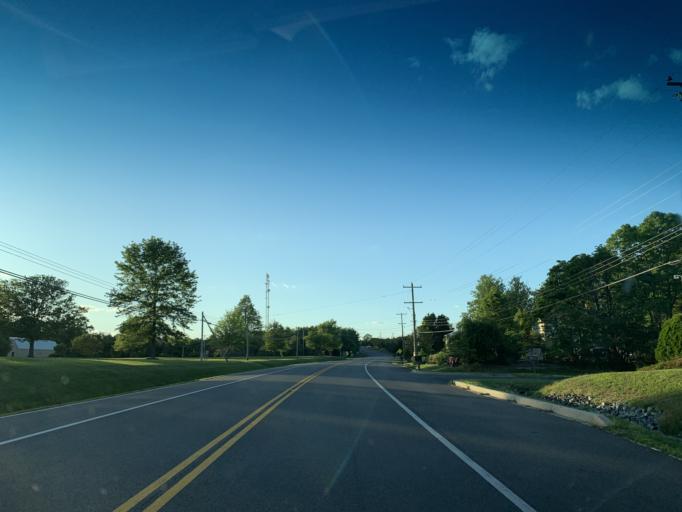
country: US
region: Maryland
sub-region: Cecil County
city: Elkton
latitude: 39.6742
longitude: -75.8585
